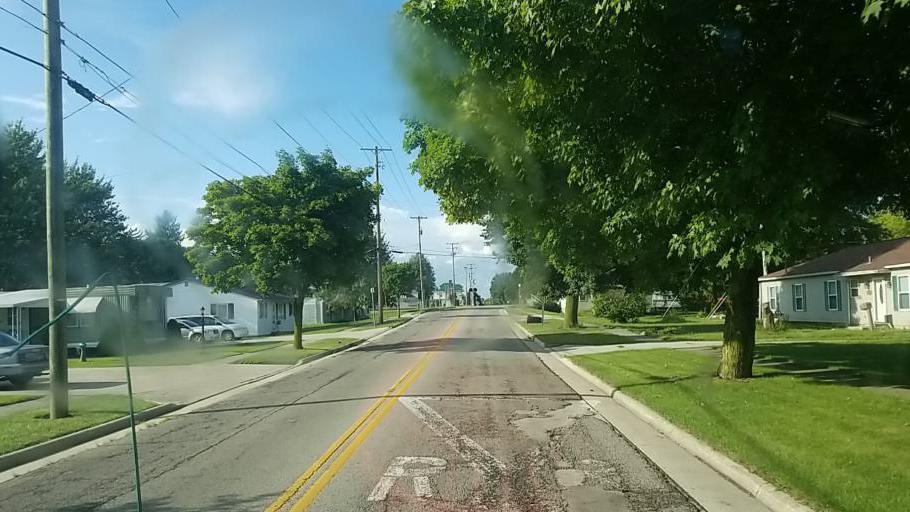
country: US
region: Ohio
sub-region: Wyandot County
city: Upper Sandusky
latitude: 40.8237
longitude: -83.2902
